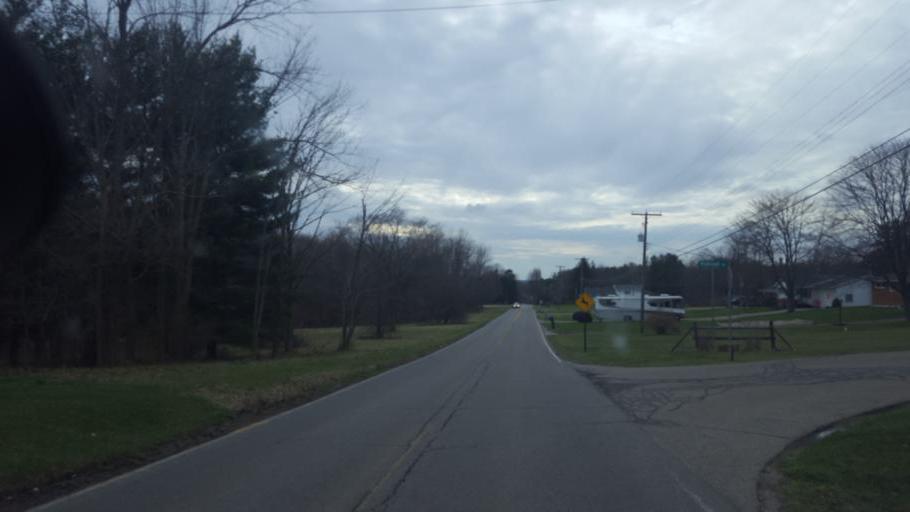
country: US
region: Ohio
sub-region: Richland County
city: Lexington
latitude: 40.6960
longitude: -82.5426
